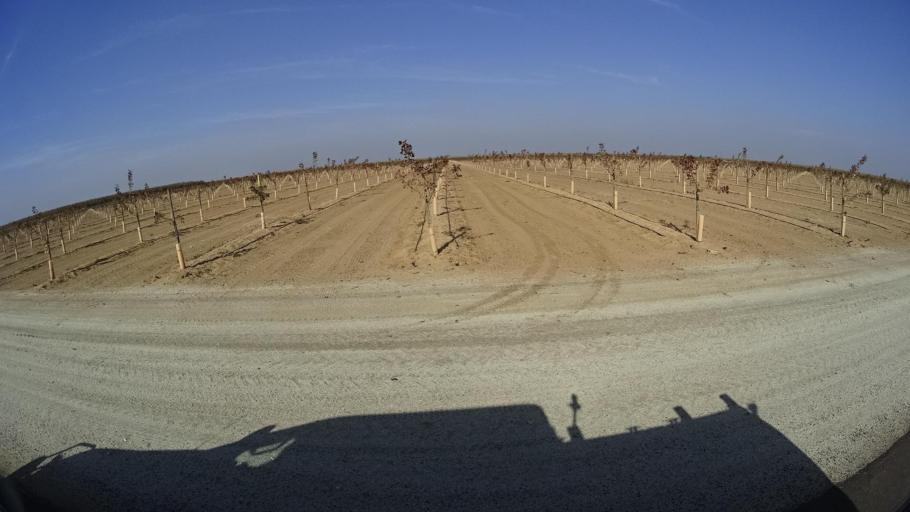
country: US
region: California
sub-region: Kern County
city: McFarland
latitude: 35.6311
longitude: -119.1901
